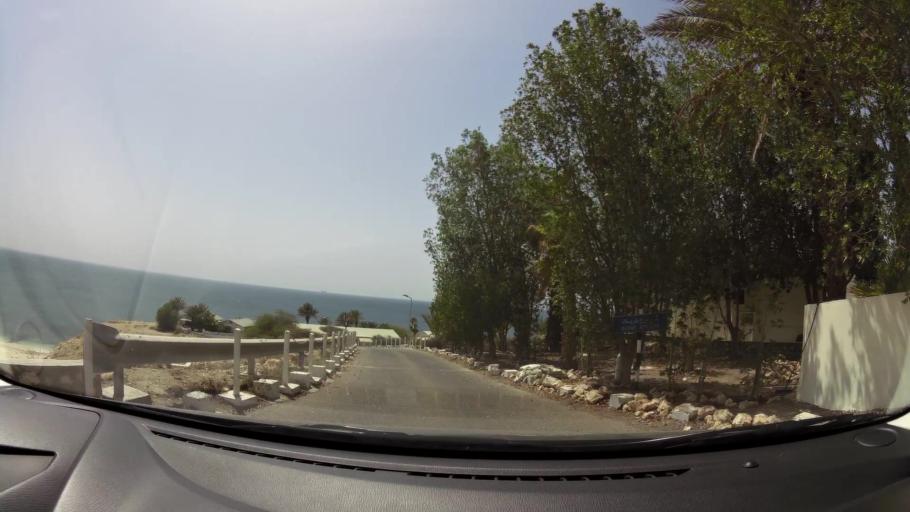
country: OM
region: Muhafazat Masqat
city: Muscat
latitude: 23.6409
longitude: 58.4932
